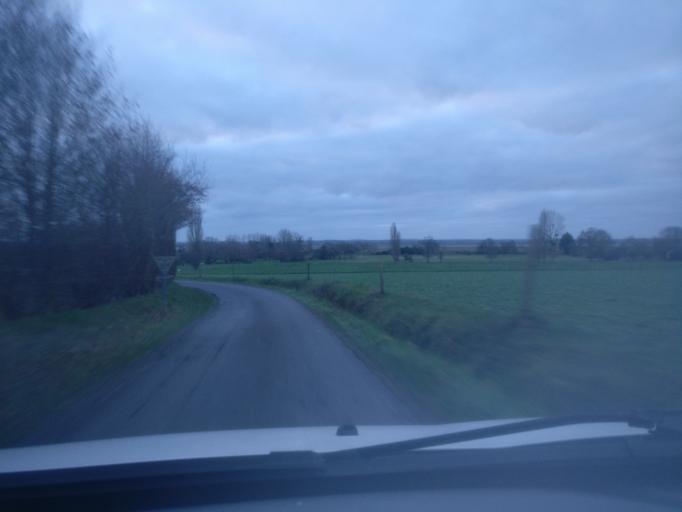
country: FR
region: Lower Normandy
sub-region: Departement de la Manche
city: Marcey-les-Greves
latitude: 48.6713
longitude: -1.4344
